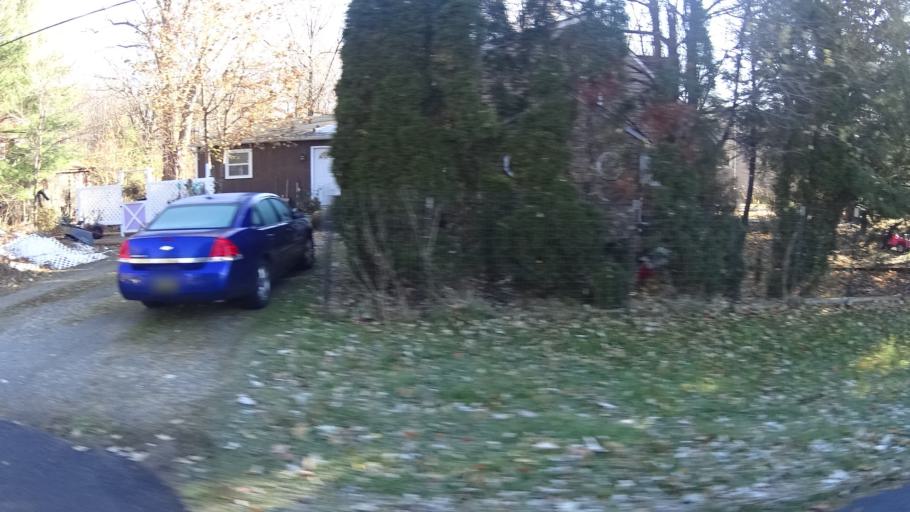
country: US
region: Ohio
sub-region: Lorain County
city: Sheffield Lake
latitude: 41.4630
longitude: -82.0986
